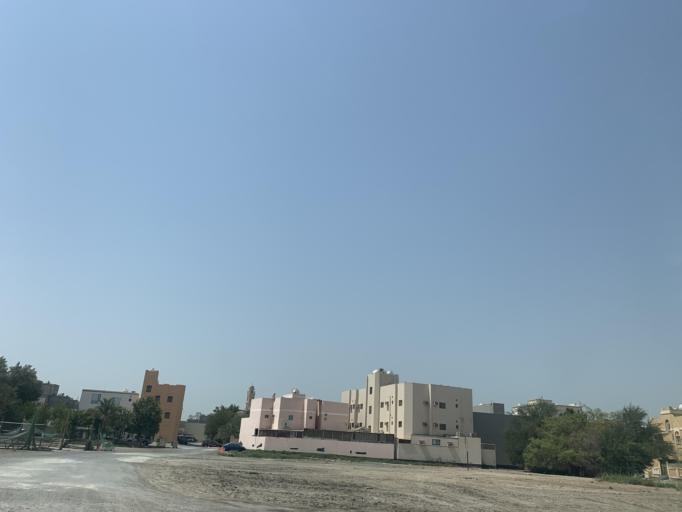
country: BH
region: Manama
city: Jidd Hafs
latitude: 26.2011
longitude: 50.5208
